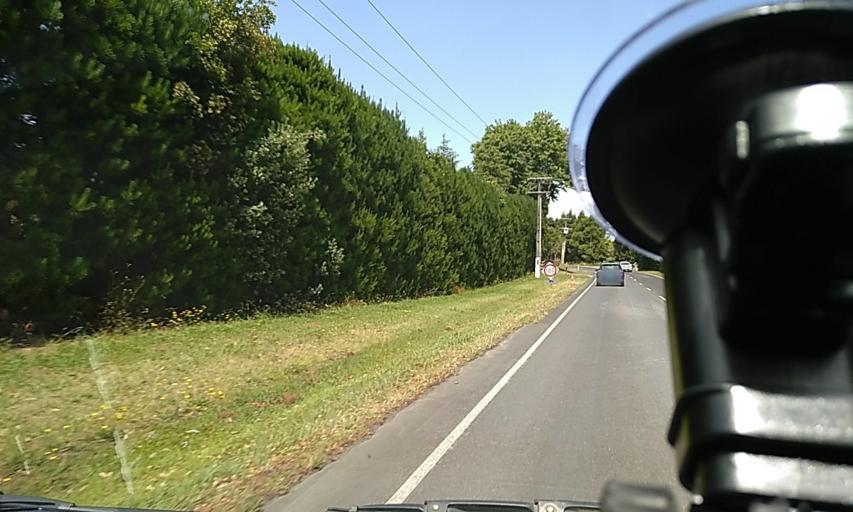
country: NZ
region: Bay of Plenty
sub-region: Western Bay of Plenty District
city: Waihi Beach
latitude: -37.4527
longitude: 175.9440
